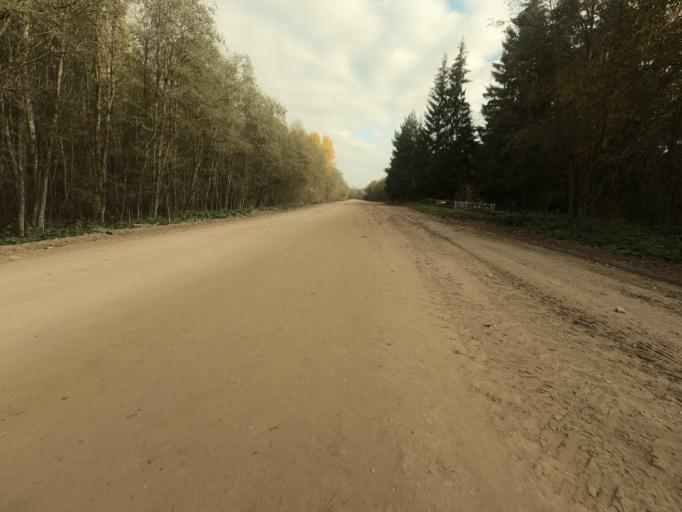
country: RU
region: Novgorod
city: Batetskiy
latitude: 58.7990
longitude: 30.6396
